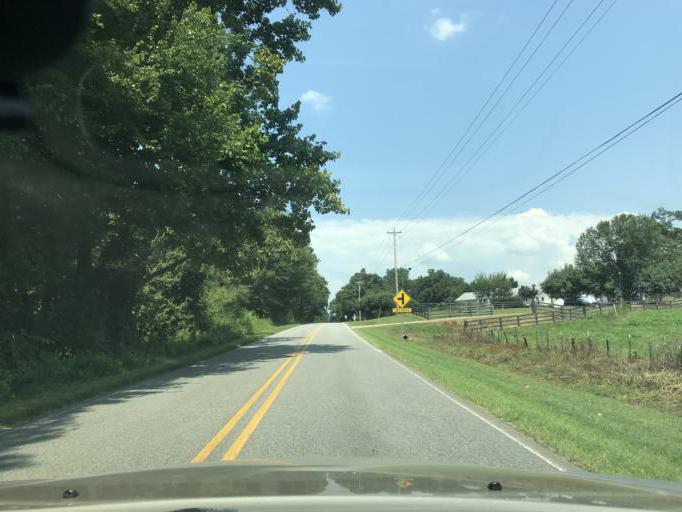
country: US
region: Georgia
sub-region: Forsyth County
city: Cumming
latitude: 34.2967
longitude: -84.1088
